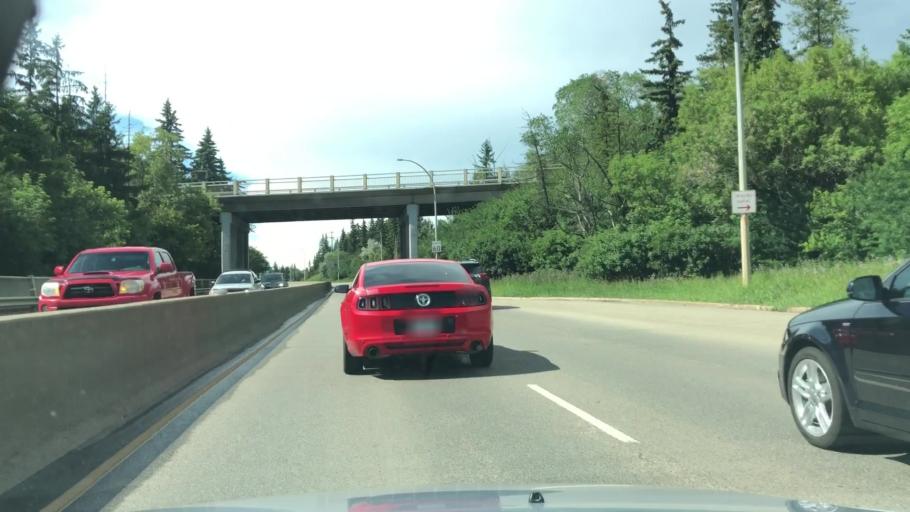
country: CA
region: Alberta
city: Edmonton
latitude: 53.5473
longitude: -113.5451
